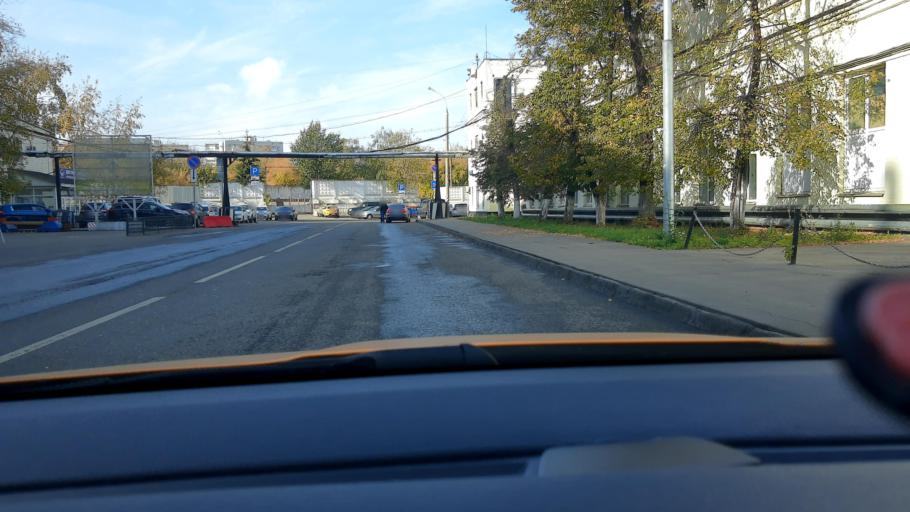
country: RU
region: Moscow
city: Lefortovo
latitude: 55.7384
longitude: 37.7167
